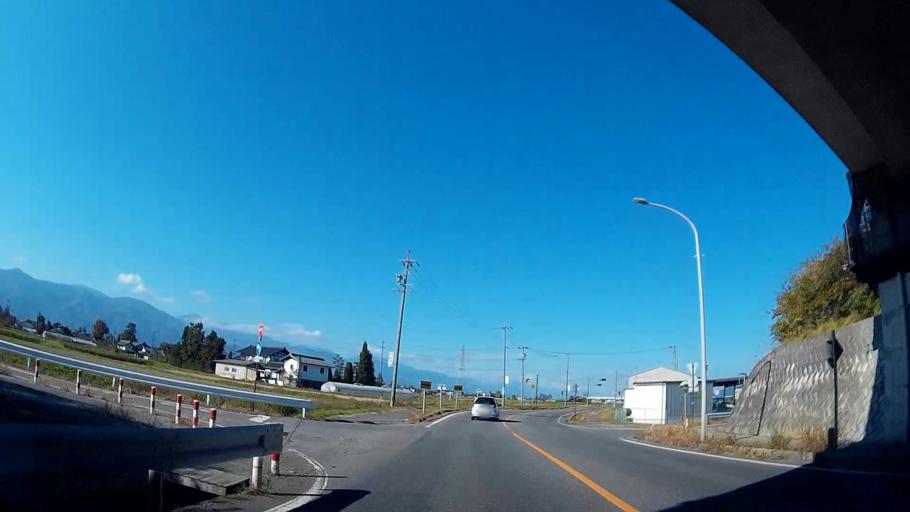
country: JP
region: Nagano
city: Matsumoto
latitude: 36.2214
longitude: 137.9338
